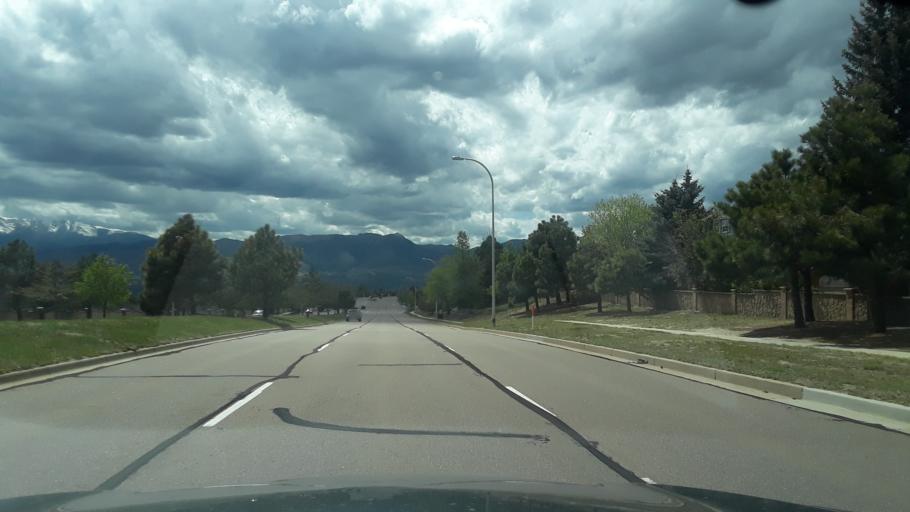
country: US
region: Colorado
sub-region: El Paso County
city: Black Forest
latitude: 38.9569
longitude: -104.7599
